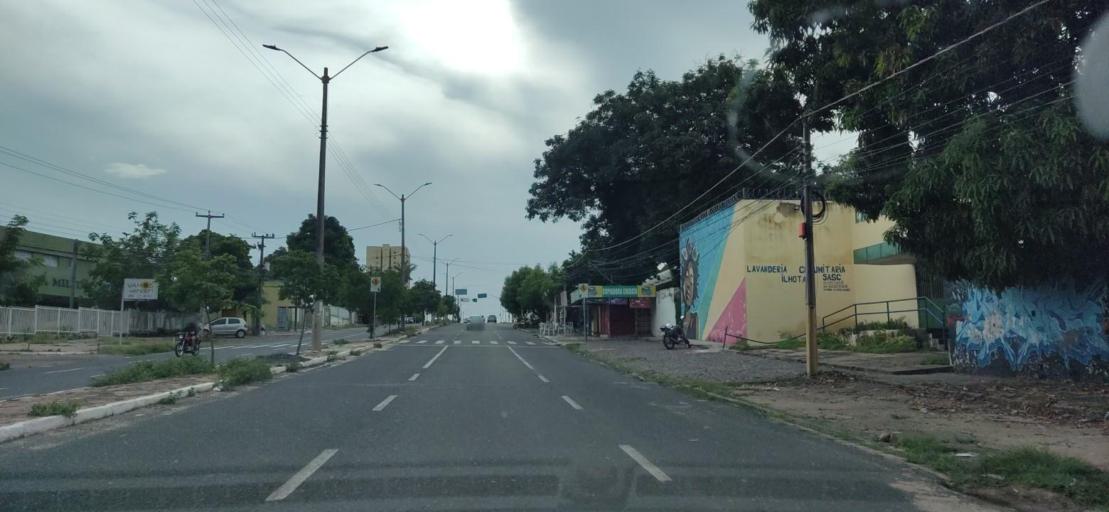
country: BR
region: Piaui
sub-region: Teresina
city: Teresina
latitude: -5.0949
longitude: -42.7865
